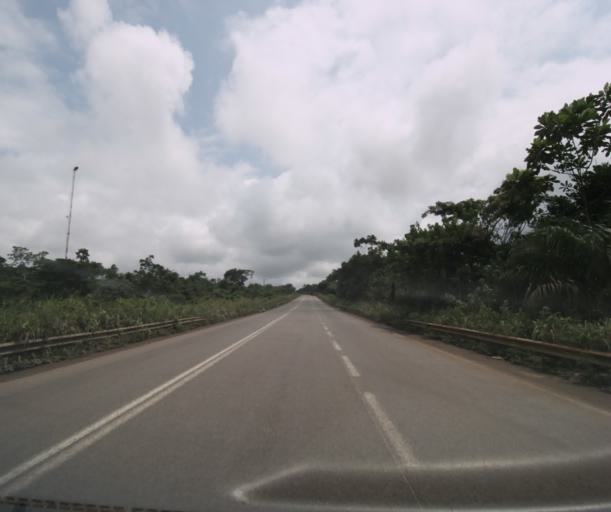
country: CM
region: Littoral
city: Edea
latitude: 3.7792
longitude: 10.1587
